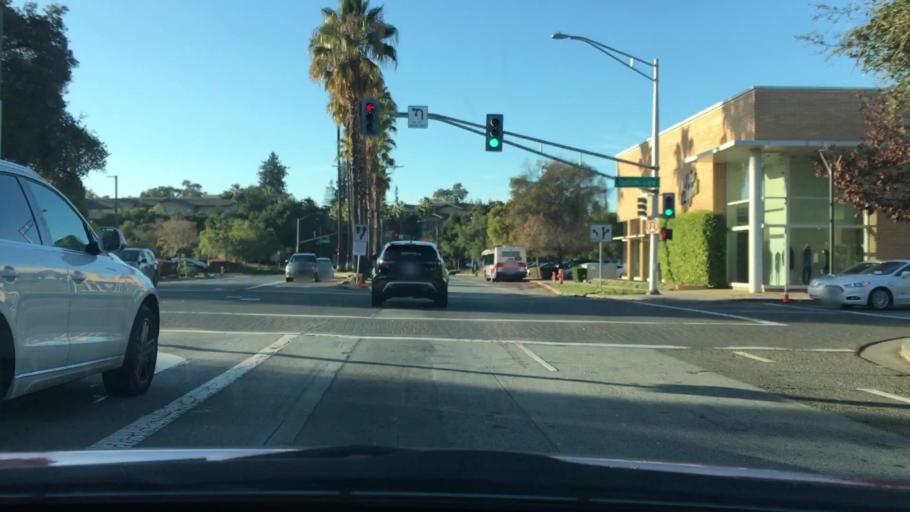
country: US
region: California
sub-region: San Mateo County
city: Menlo Park
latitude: 37.4400
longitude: -122.1724
